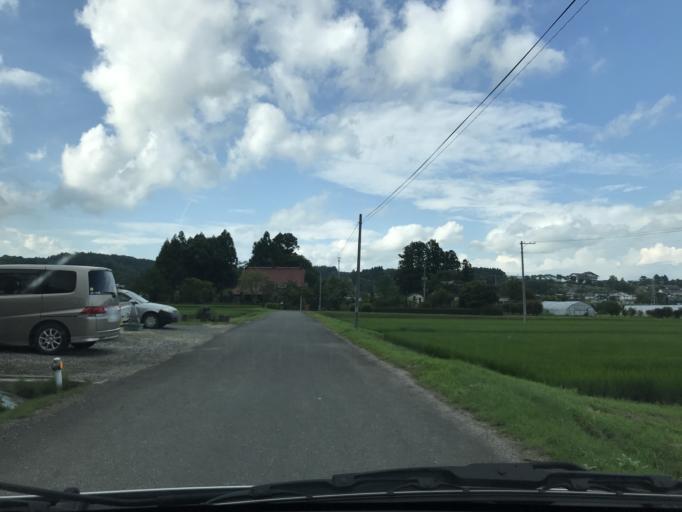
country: JP
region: Iwate
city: Ichinoseki
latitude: 39.0113
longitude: 141.1021
